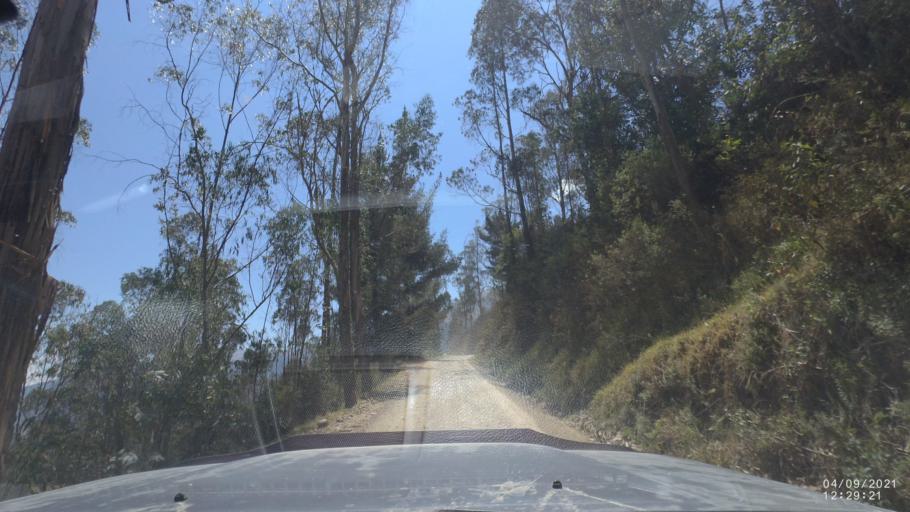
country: BO
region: Cochabamba
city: Colchani
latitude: -17.2240
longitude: -66.5254
